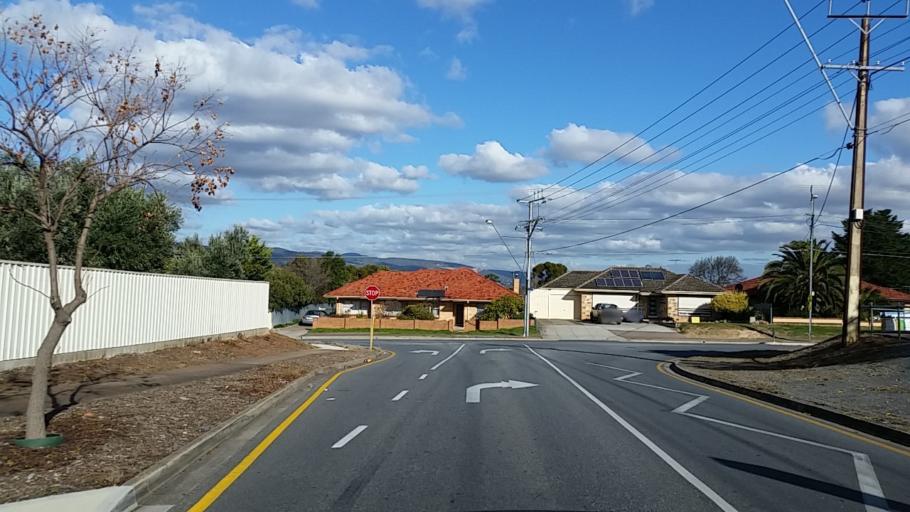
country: AU
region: South Australia
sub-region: Campbelltown
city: Paradise
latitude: -34.8567
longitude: 138.6720
